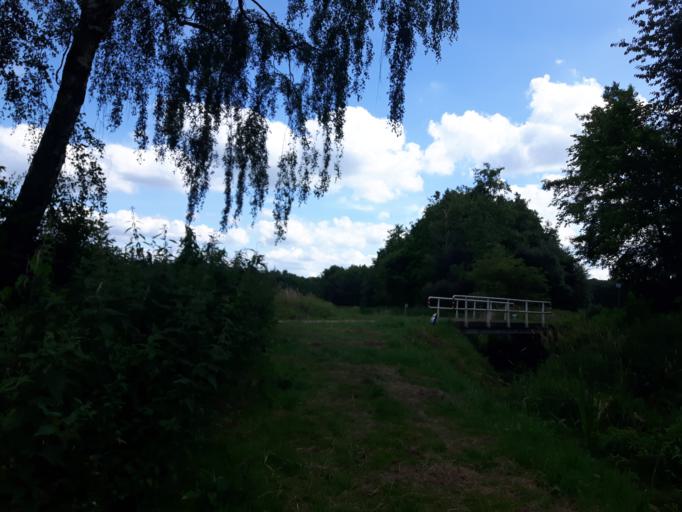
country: NL
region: Overijssel
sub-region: Gemeente Haaksbergen
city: Haaksbergen
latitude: 52.1884
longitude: 6.7708
